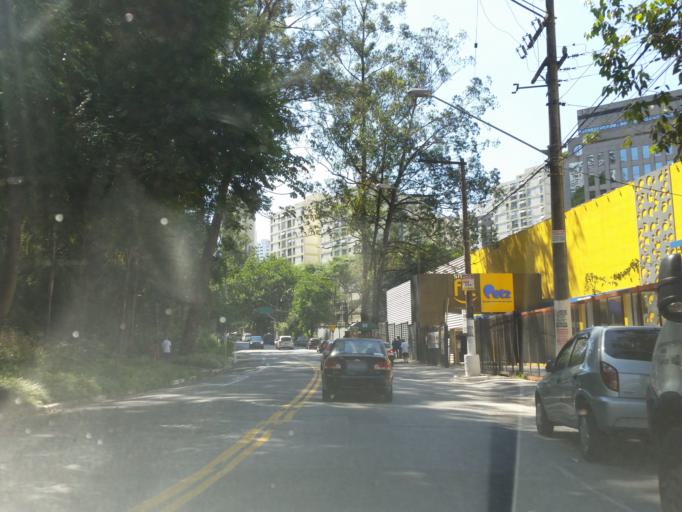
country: BR
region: Sao Paulo
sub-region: Taboao Da Serra
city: Taboao da Serra
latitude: -23.6297
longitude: -46.7376
